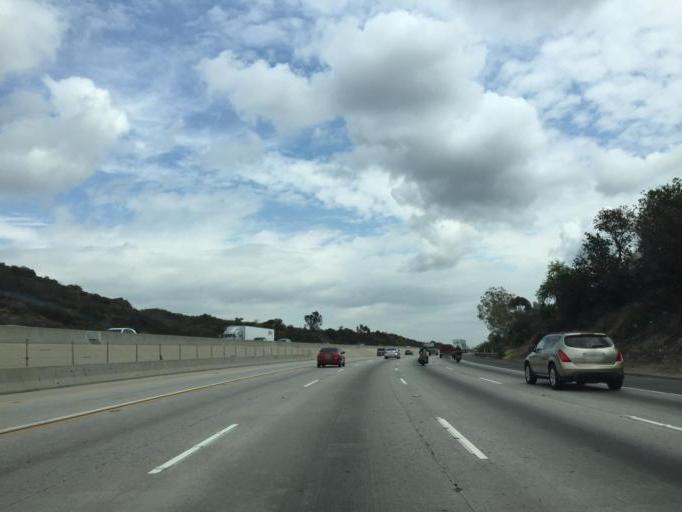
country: US
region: California
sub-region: Los Angeles County
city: La Canada Flintridge
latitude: 34.1480
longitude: -118.1973
